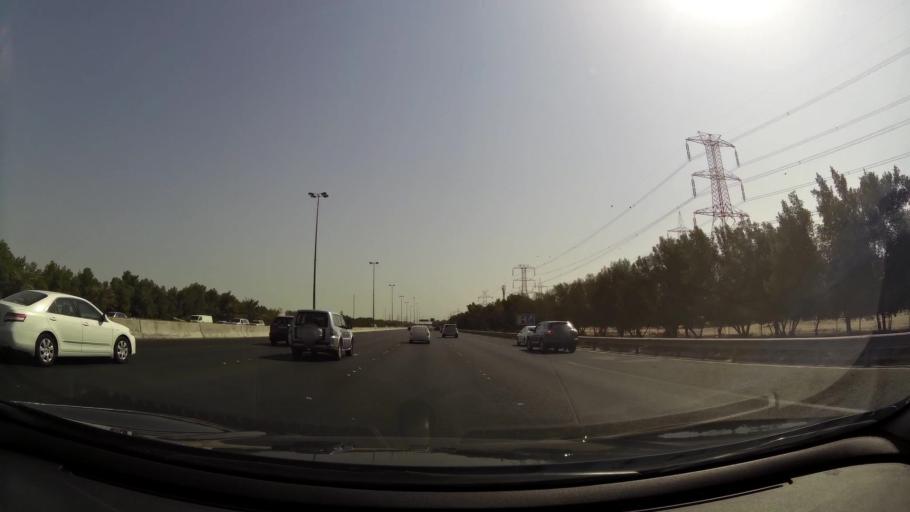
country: KW
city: Bayan
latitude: 29.2869
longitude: 48.0312
